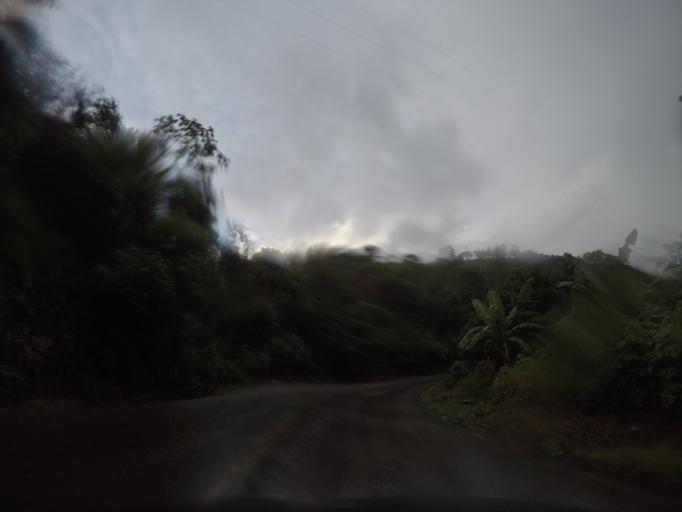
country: MX
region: Oaxaca
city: San Gabriel Mixtepec
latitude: 16.0724
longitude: -97.0786
